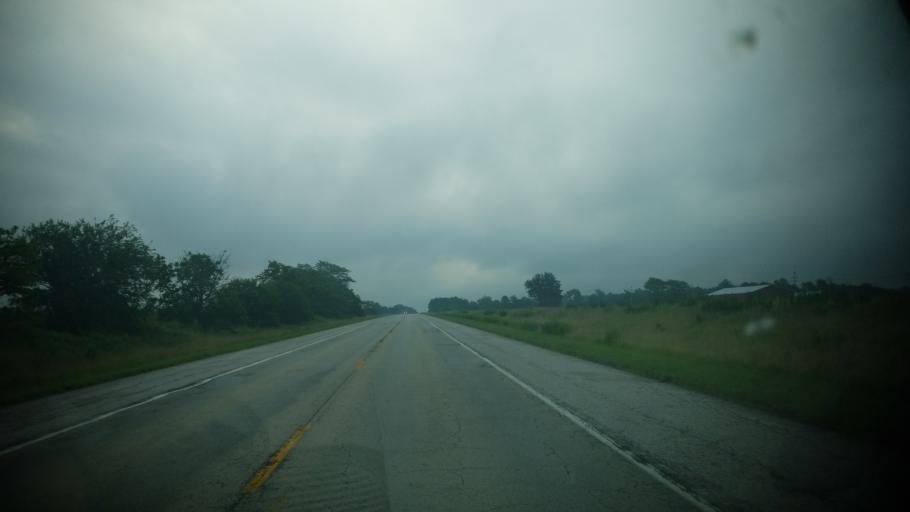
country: US
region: Illinois
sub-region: Clay County
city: Flora
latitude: 38.6773
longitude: -88.4093
